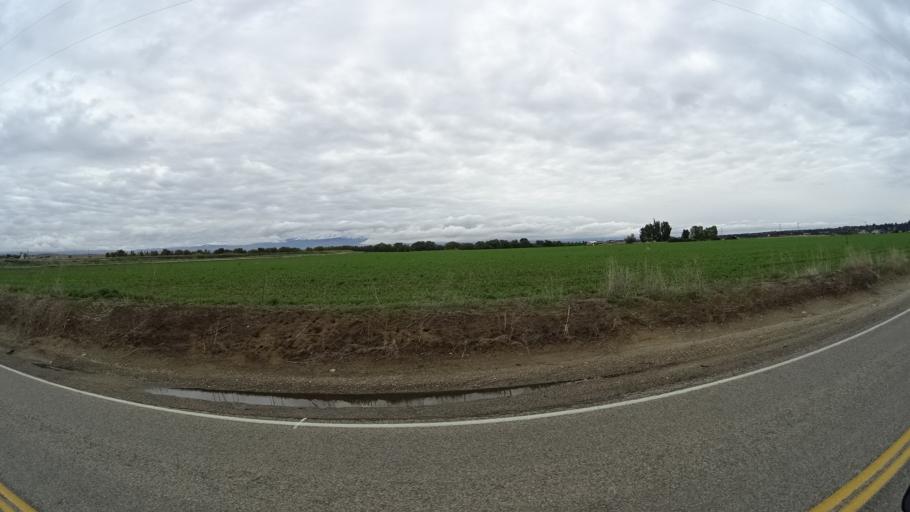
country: US
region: Idaho
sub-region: Ada County
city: Star
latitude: 43.7105
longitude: -116.4434
